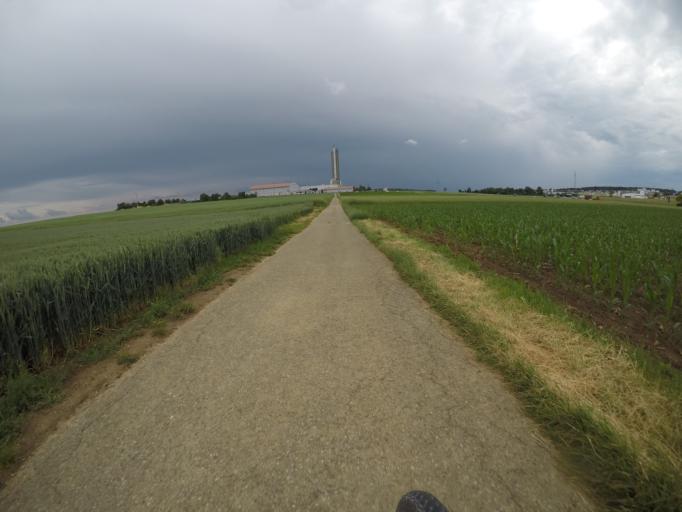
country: DE
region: Baden-Wuerttemberg
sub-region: Tuebingen Region
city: Ulm
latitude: 48.4391
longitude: 9.9810
